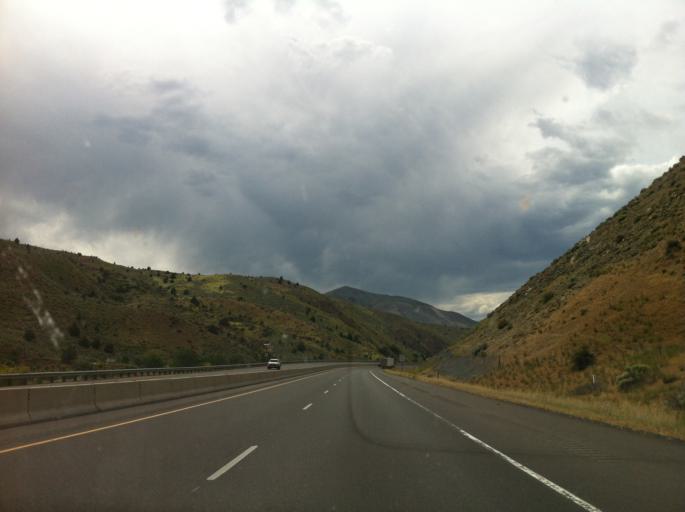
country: US
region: Idaho
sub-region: Washington County
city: Weiser
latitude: 44.4845
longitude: -117.3545
